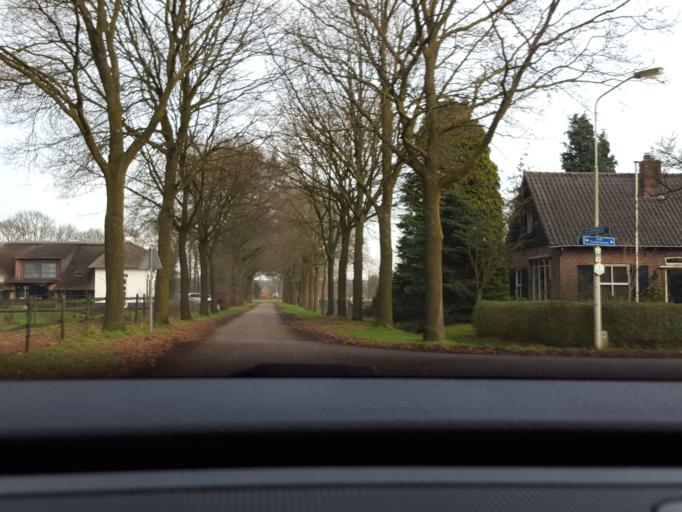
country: NL
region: Gelderland
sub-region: Gemeente Lochem
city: Almen
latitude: 52.1129
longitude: 6.3123
